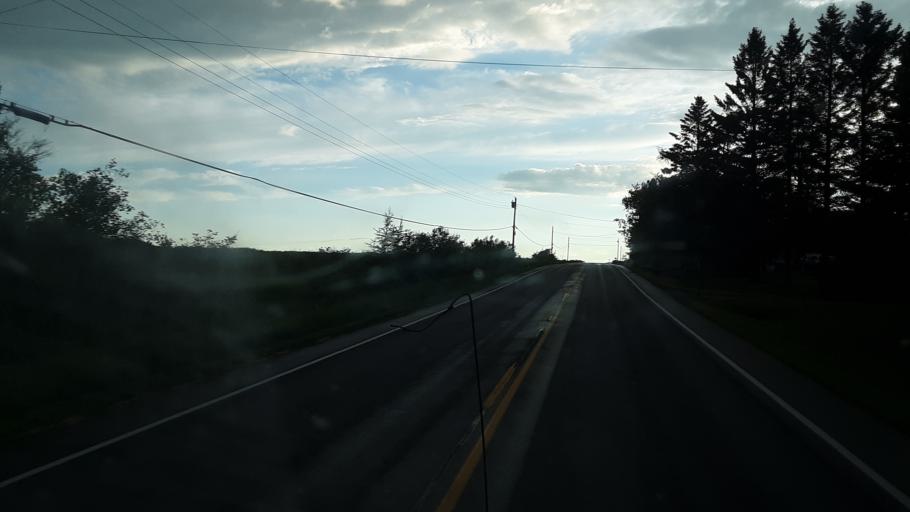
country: US
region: Maine
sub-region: Aroostook County
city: Easton
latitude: 46.6754
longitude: -67.9540
